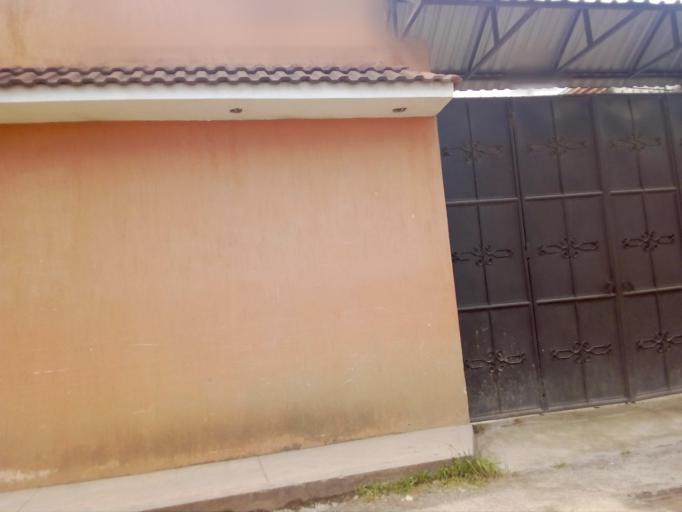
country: GT
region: Quetzaltenango
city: Quetzaltenango
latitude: 14.8525
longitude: -91.5087
